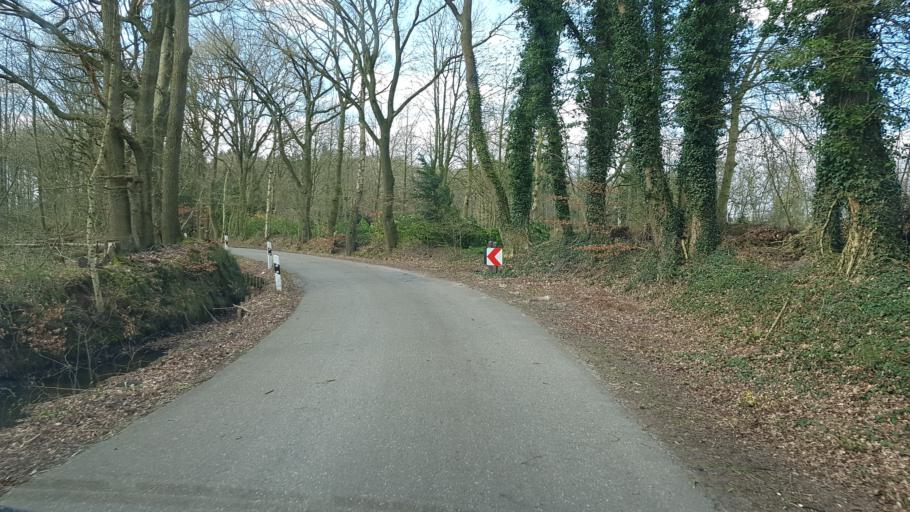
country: DE
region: Lower Saxony
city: Edewecht
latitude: 53.1558
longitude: 7.9453
